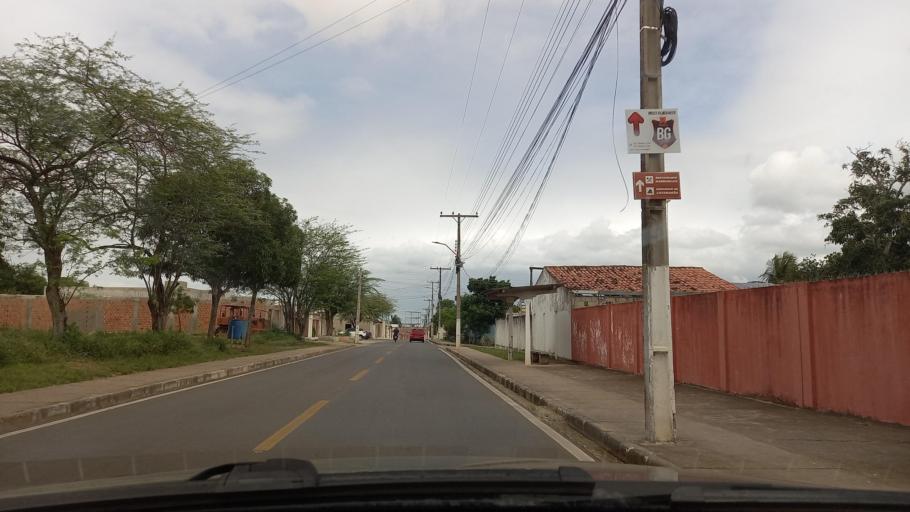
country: BR
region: Sergipe
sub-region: Caninde De Sao Francisco
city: Caninde de Sao Francisco
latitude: -9.6114
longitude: -37.7635
